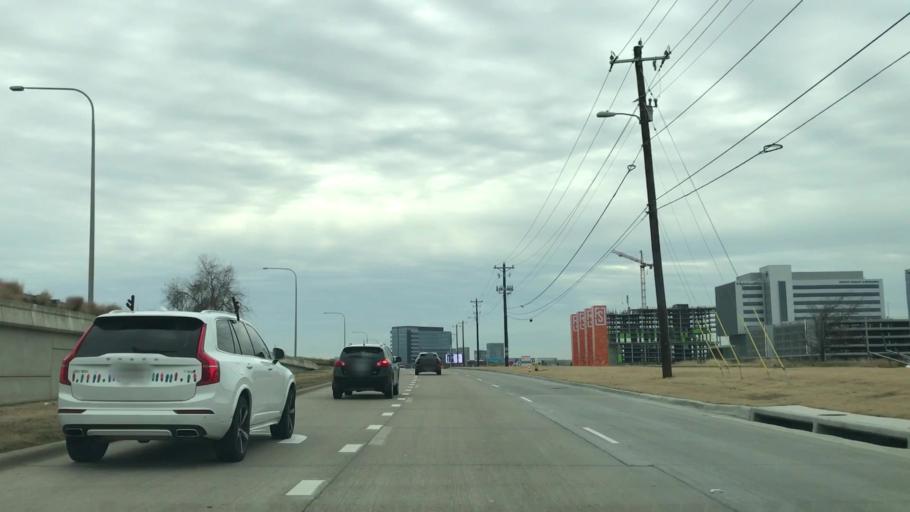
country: US
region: Texas
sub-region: Collin County
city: Frisco
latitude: 33.1142
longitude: -96.8239
